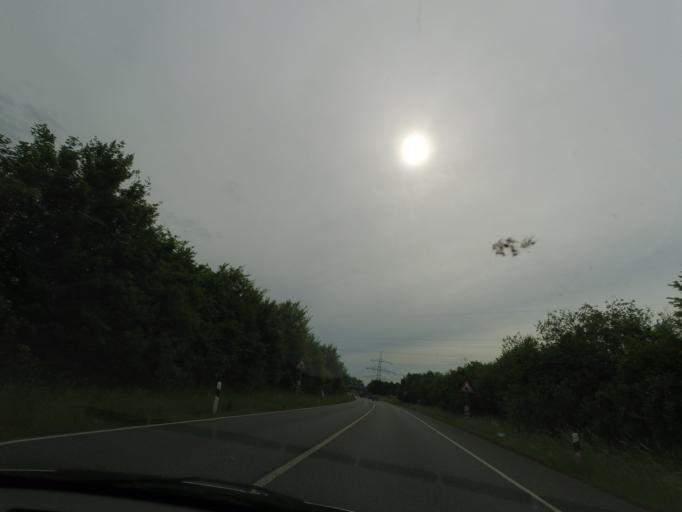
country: DE
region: Hesse
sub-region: Regierungsbezirk Giessen
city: Kirchhain
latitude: 50.8132
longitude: 8.9484
